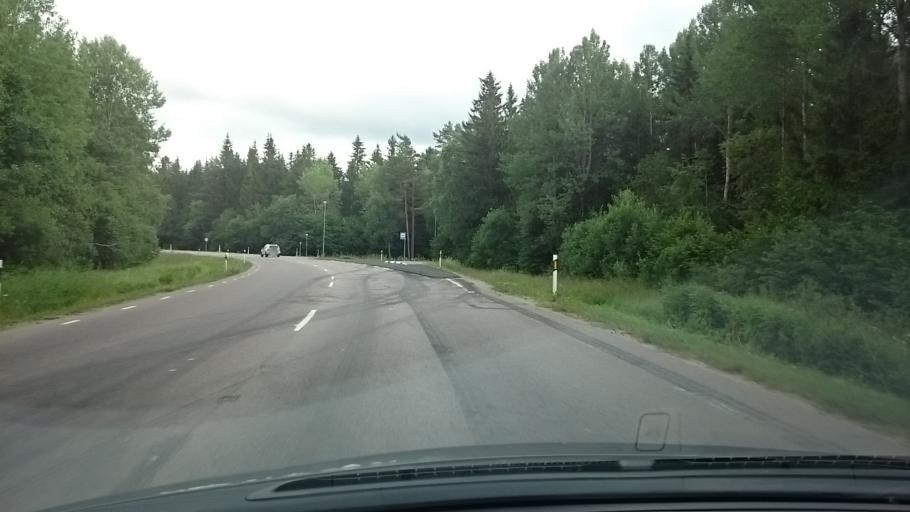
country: EE
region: Harju
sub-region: Saku vald
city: Saku
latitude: 59.3032
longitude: 24.6378
